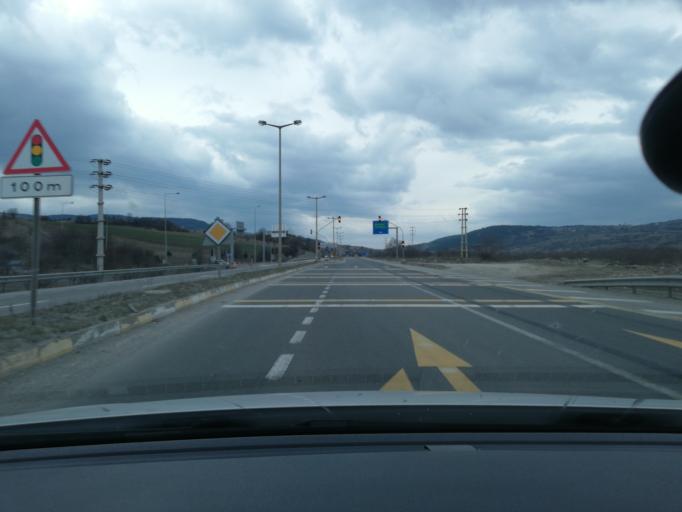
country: TR
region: Bolu
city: Yenicaga
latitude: 40.7728
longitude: 32.0090
